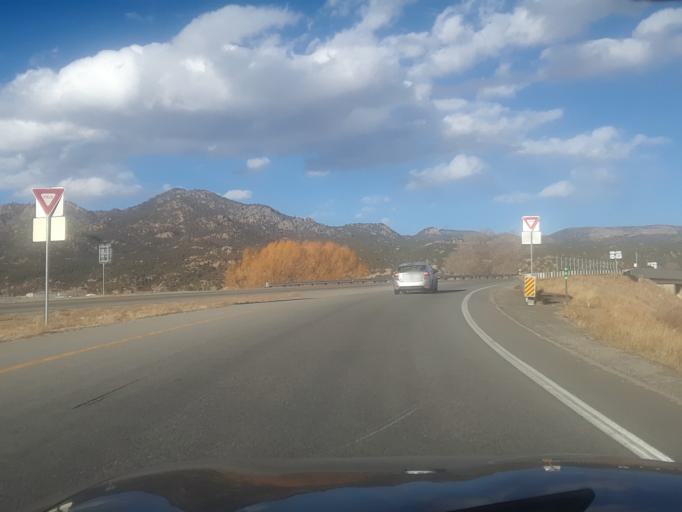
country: US
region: Colorado
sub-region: Chaffee County
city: Buena Vista
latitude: 38.8096
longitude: -106.1152
